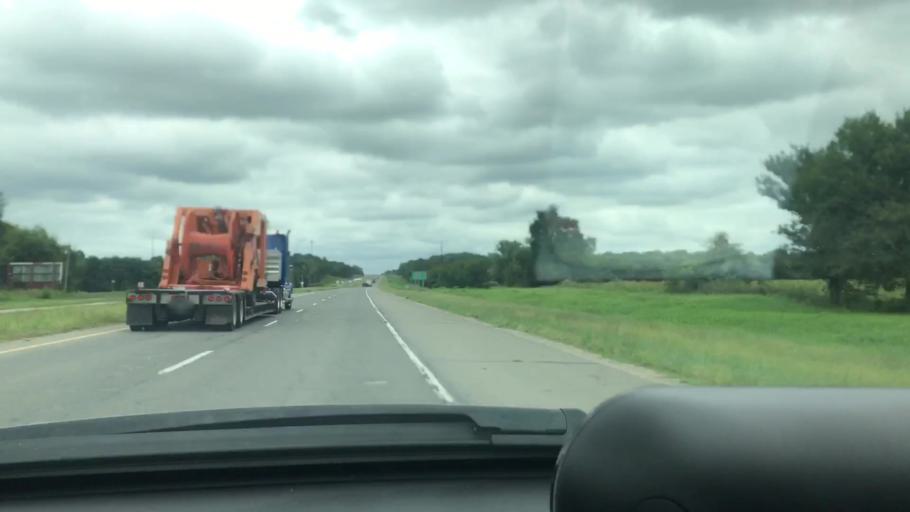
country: US
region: Oklahoma
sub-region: Muskogee County
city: Muskogee
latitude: 35.8148
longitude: -95.4027
